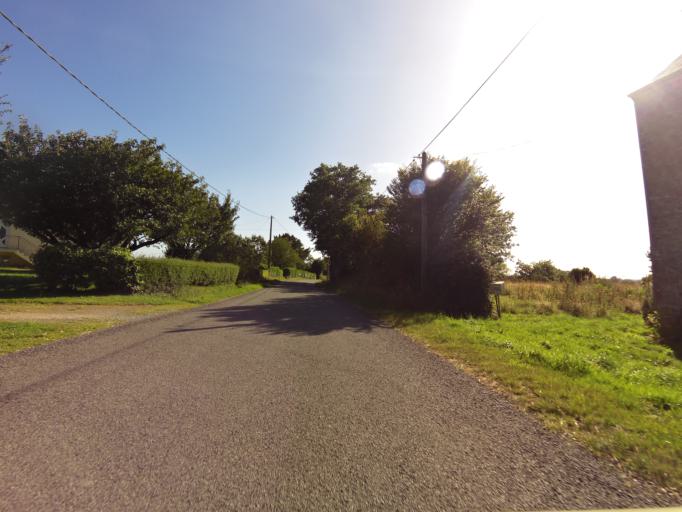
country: FR
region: Brittany
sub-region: Departement du Morbihan
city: Caden
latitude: 47.6341
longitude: -2.2701
